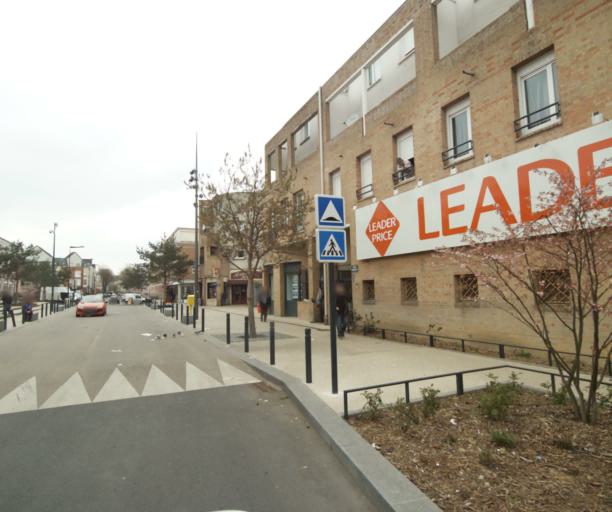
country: FR
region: Ile-de-France
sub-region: Departement du Val-d'Oise
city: Vaureal
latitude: 49.0469
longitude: 2.0341
